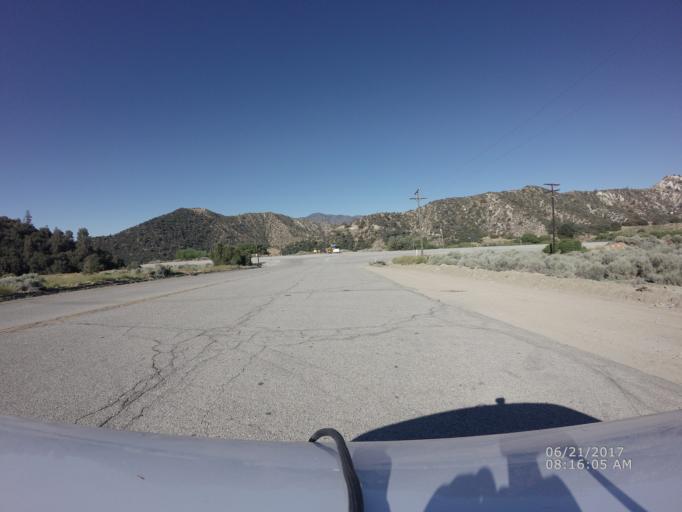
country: US
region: California
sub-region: Kern County
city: Lebec
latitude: 34.7074
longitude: -118.7972
